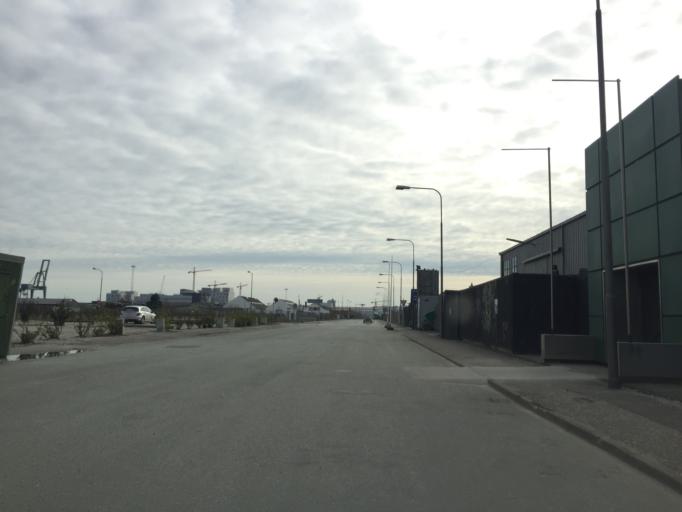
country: DK
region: Capital Region
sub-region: Gentofte Kommune
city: Charlottenlund
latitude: 55.7186
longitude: 12.5984
